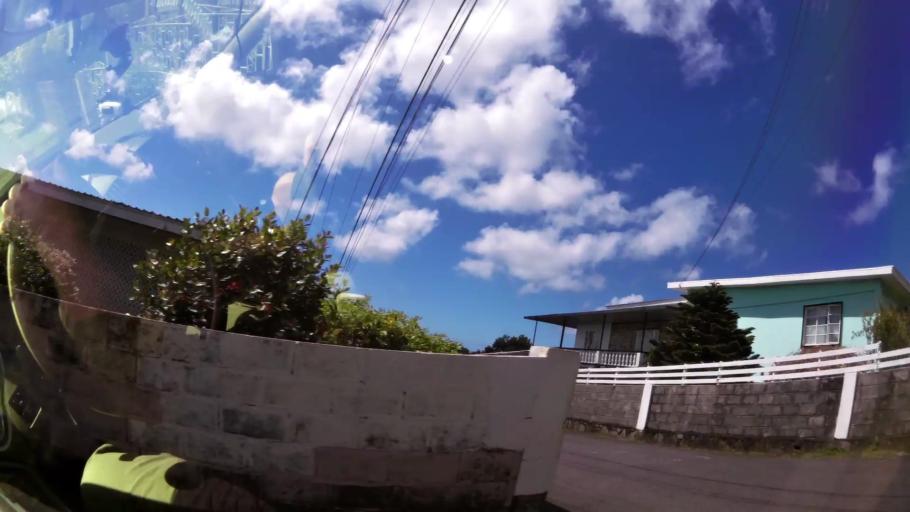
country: VC
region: Saint George
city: Kingstown
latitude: 13.1414
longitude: -61.2243
